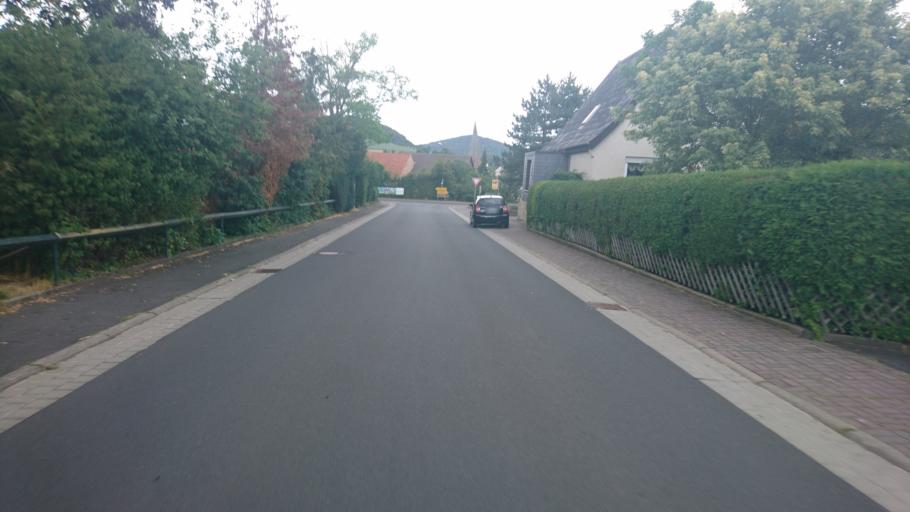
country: DE
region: Hesse
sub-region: Regierungsbezirk Kassel
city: Rasdorf
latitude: 50.7163
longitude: 9.9003
